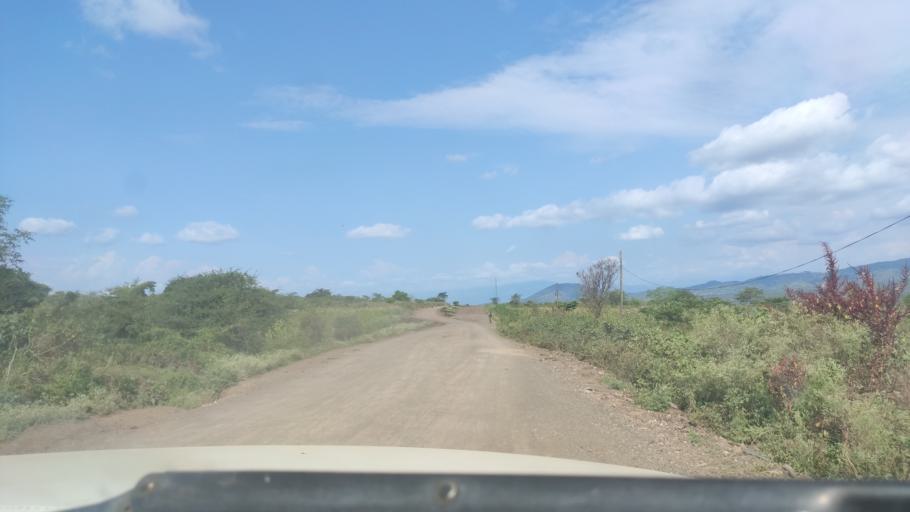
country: ET
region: Southern Nations, Nationalities, and People's Region
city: Felege Neway
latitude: 6.3947
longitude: 37.1032
